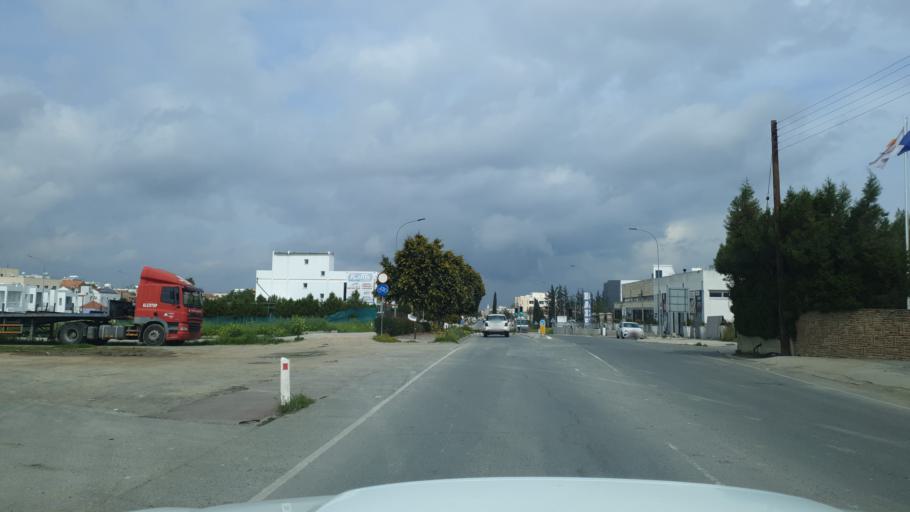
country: CY
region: Lefkosia
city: Geri
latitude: 35.0935
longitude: 33.3792
